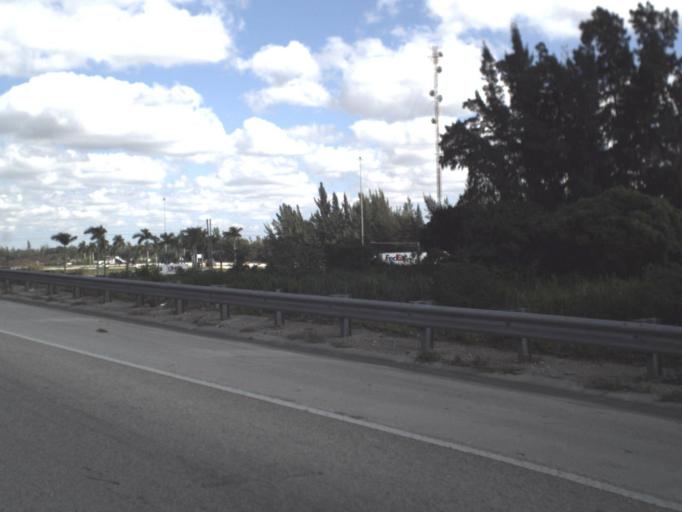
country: US
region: Florida
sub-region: Miami-Dade County
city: Palm Springs North
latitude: 25.8988
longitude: -80.3860
